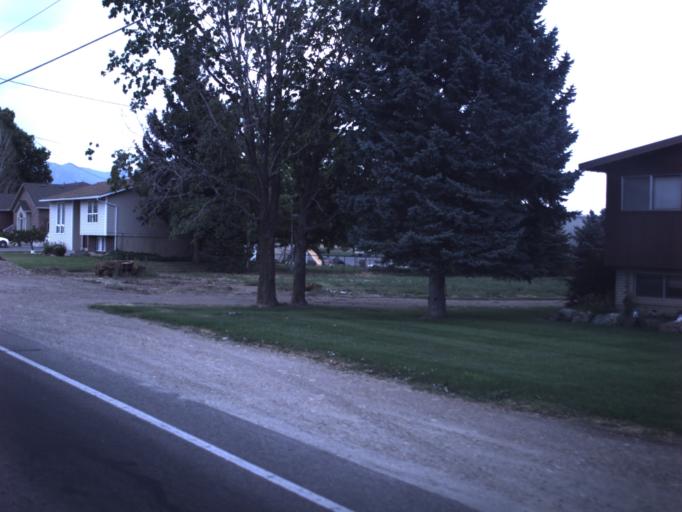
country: US
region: Utah
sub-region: Davis County
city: West Point
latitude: 41.1181
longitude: -112.0813
